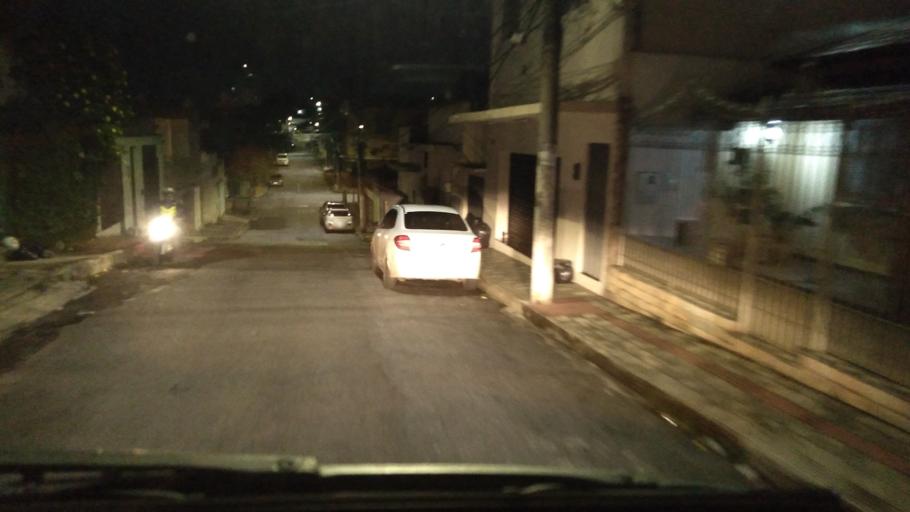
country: BR
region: Minas Gerais
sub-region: Belo Horizonte
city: Belo Horizonte
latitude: -19.8983
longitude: -43.9722
